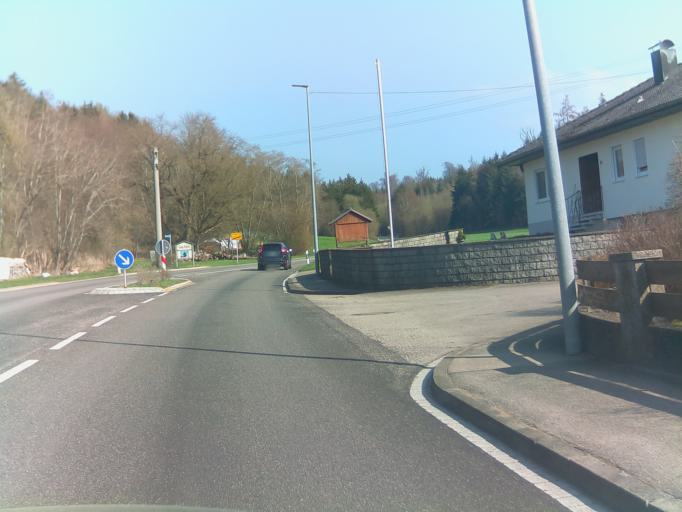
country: DE
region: Bavaria
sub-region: Swabia
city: Unterroth
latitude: 48.1959
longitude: 10.1820
